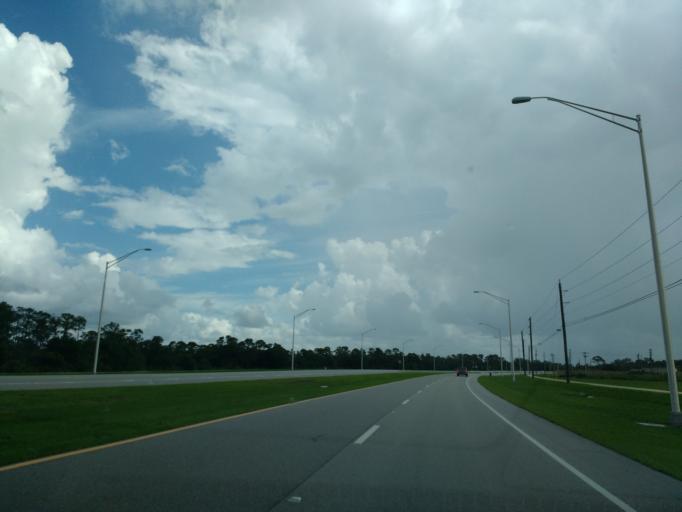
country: US
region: Florida
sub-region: Lee County
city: Burnt Store Marina
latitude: 26.7973
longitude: -82.0376
